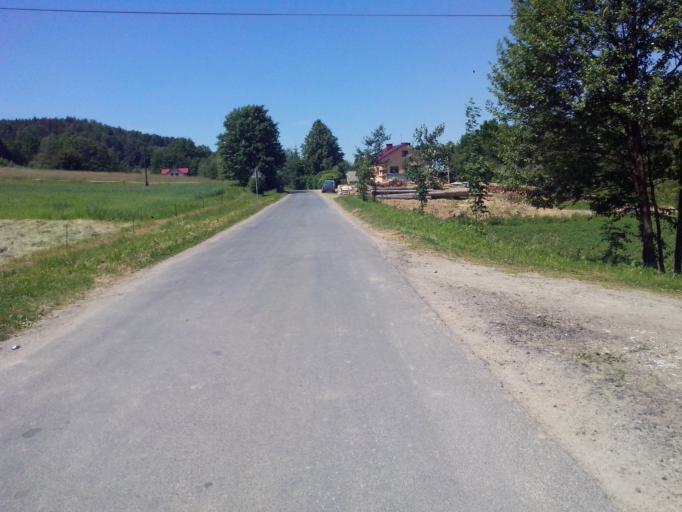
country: PL
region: Subcarpathian Voivodeship
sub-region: Powiat krosnienski
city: Wojaszowka
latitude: 49.7962
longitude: 21.7076
